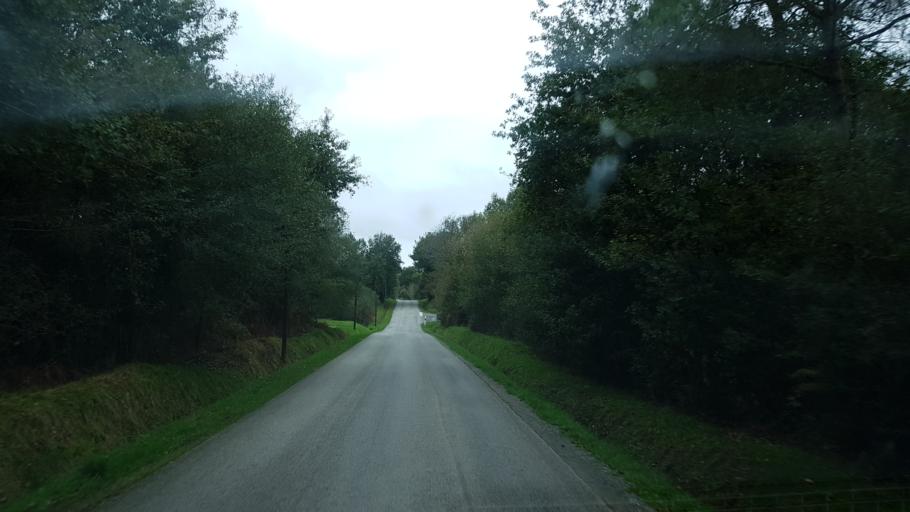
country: FR
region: Brittany
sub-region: Departement du Morbihan
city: Serent
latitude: 47.7800
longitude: -2.4768
